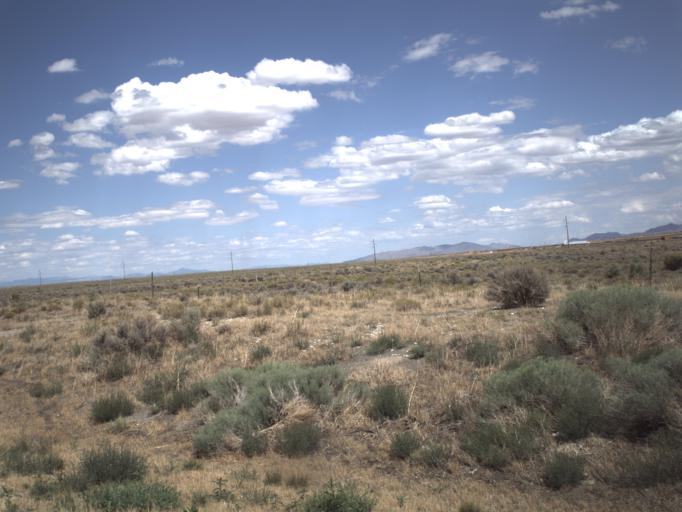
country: US
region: Utah
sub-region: Millard County
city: Delta
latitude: 39.2669
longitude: -112.4518
